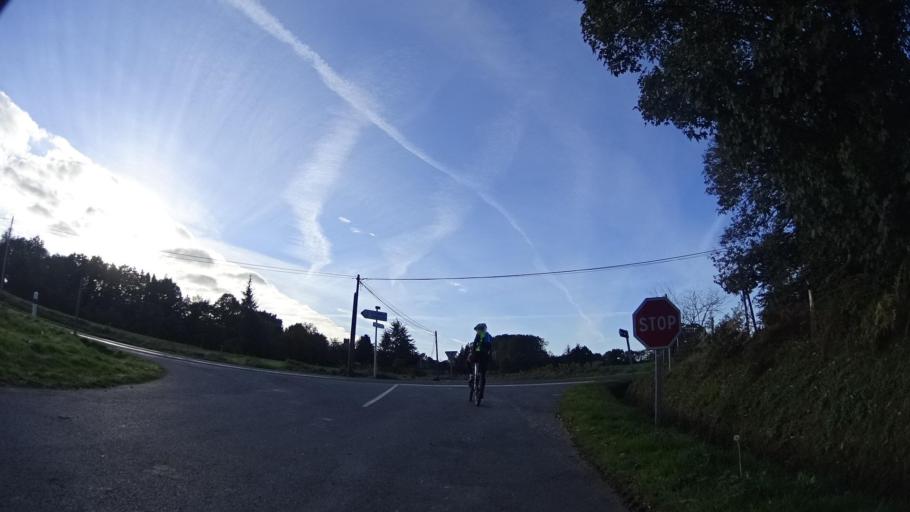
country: FR
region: Brittany
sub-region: Departement des Cotes-d'Armor
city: Evran
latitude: 48.3448
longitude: -1.9398
